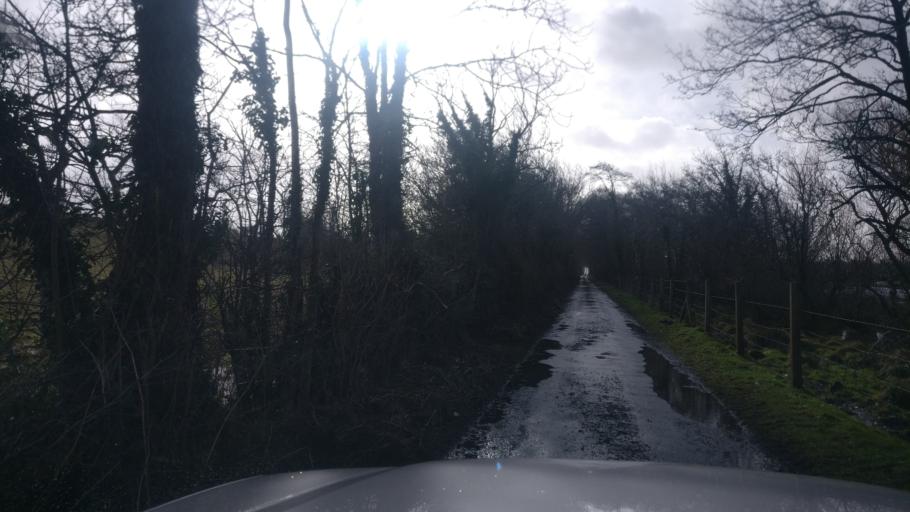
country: IE
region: Connaught
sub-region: County Galway
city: Loughrea
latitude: 53.2805
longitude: -8.5958
